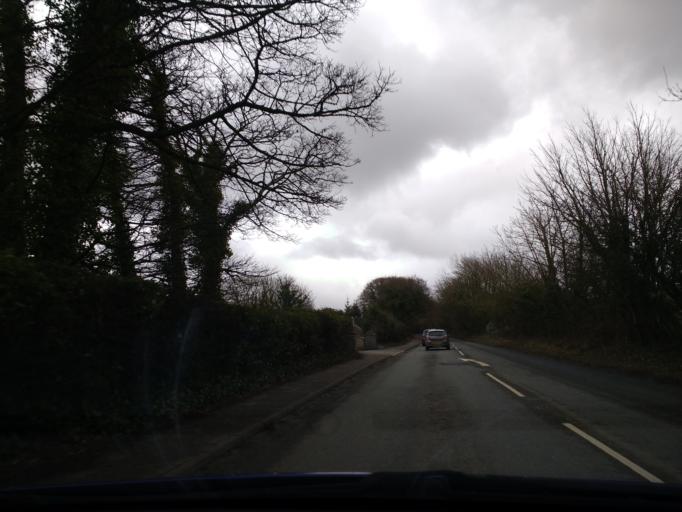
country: GB
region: England
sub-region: Cumbria
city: Maryport
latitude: 54.7101
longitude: -3.4740
